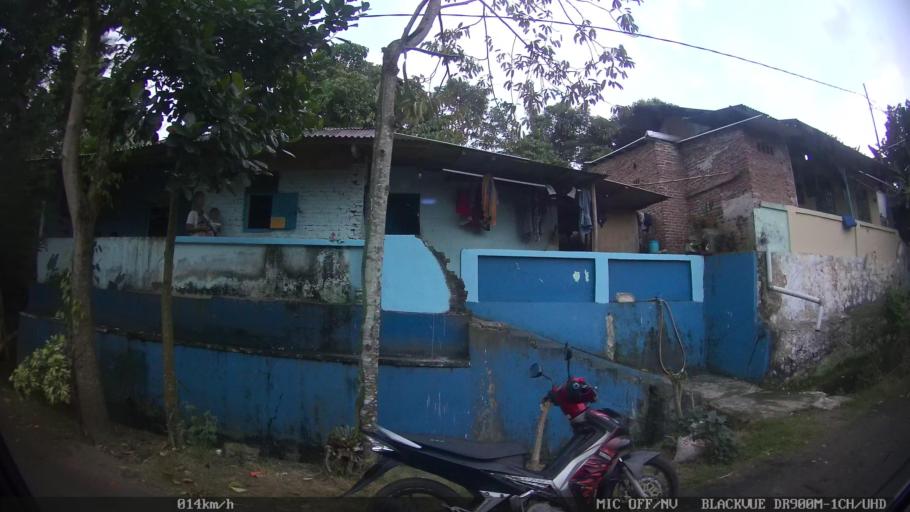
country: ID
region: Lampung
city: Bandarlampung
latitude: -5.4379
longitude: 105.2851
